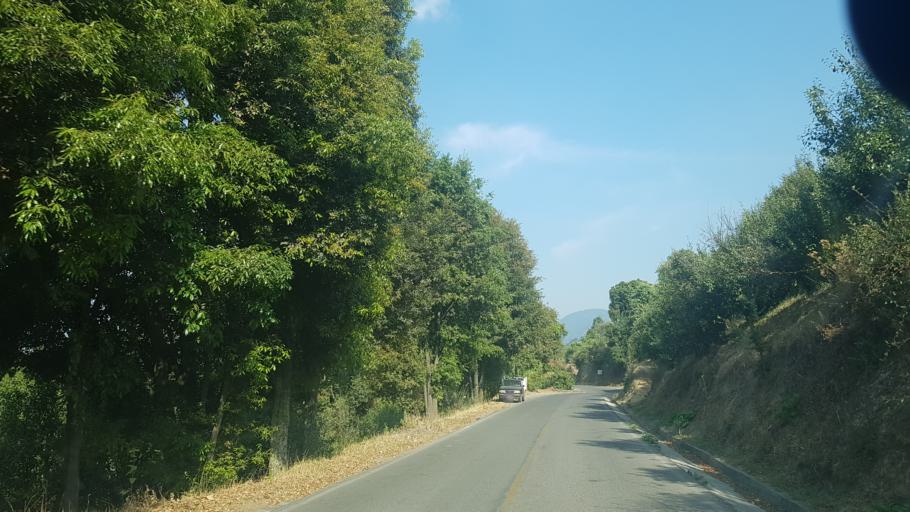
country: MX
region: Puebla
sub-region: Tochimilco
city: Santa Cruz Cuautomatitla
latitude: 18.8885
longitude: -98.6671
